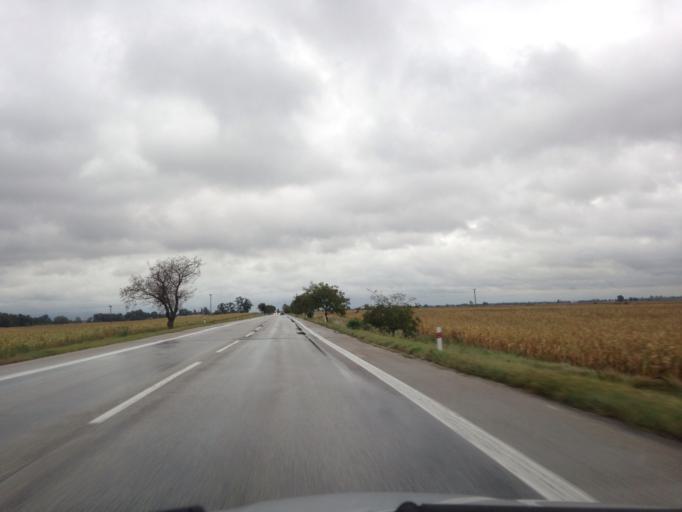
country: SK
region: Nitriansky
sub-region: Okres Komarno
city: Hurbanovo
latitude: 47.8231
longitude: 18.1773
